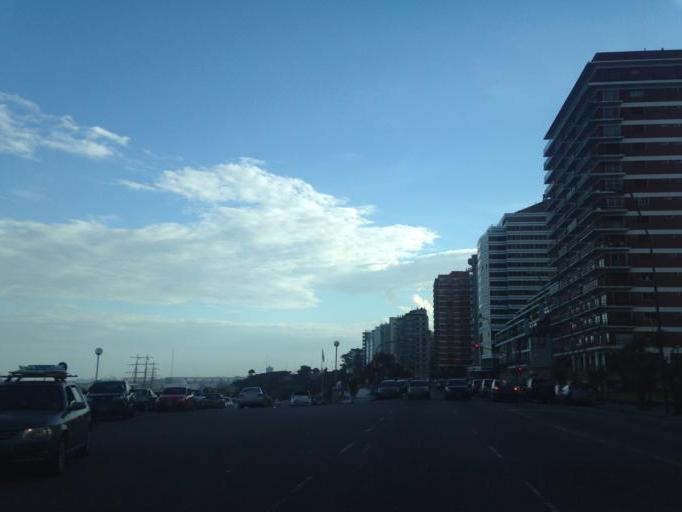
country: AR
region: Buenos Aires
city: Mar del Plata
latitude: -38.0262
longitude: -57.5323
